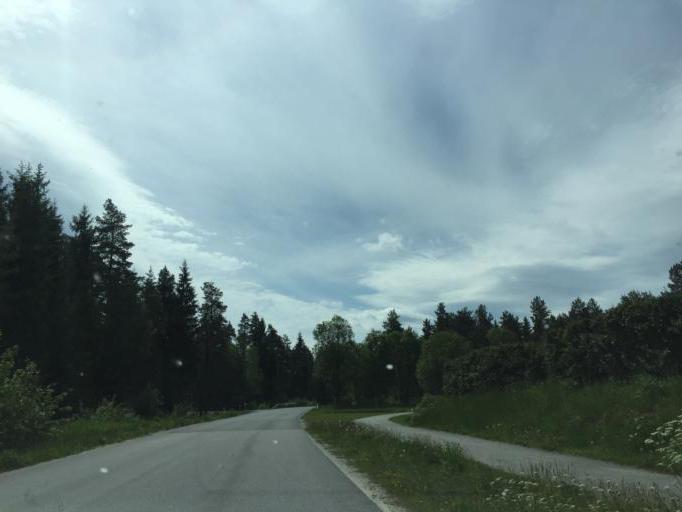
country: NO
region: Akershus
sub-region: Nes
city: Fjellfoten
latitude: 60.0896
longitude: 11.4782
